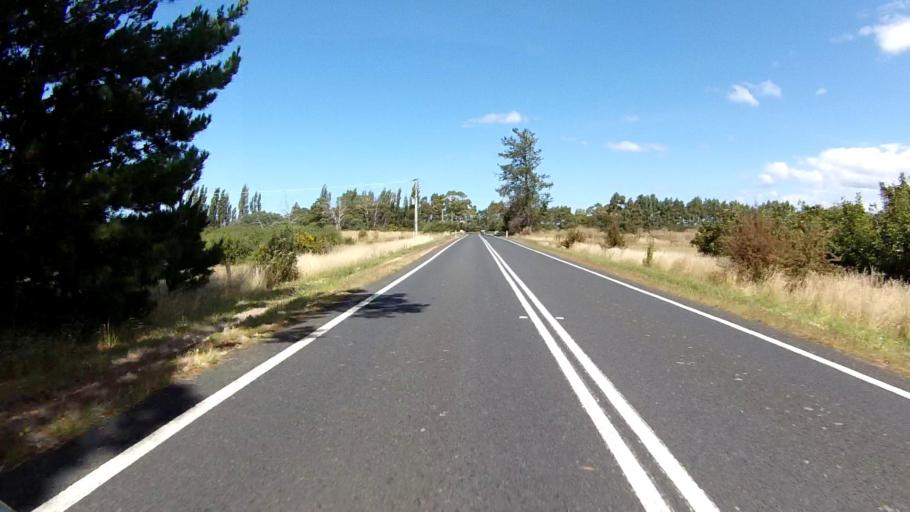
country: AU
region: Tasmania
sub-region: Break O'Day
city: St Helens
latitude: -42.0662
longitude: 148.0638
